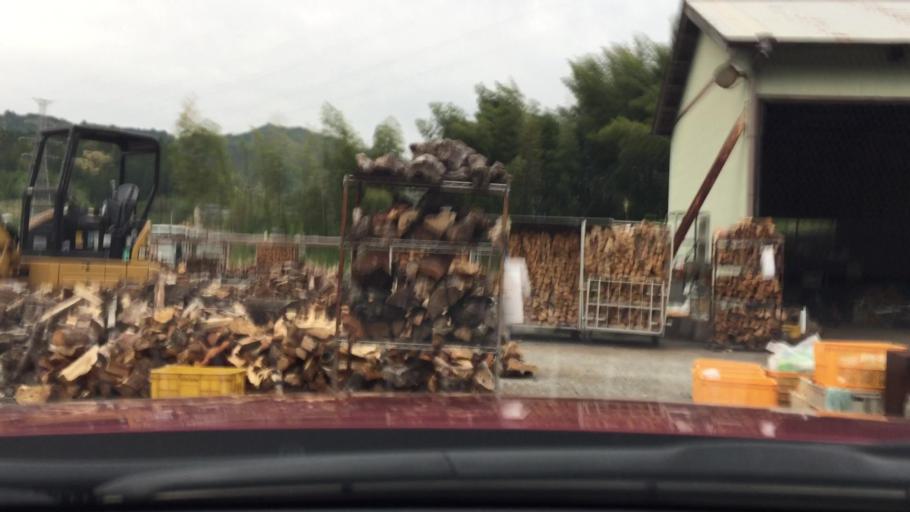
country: JP
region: Kochi
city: Ino
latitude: 33.5276
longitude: 133.3456
